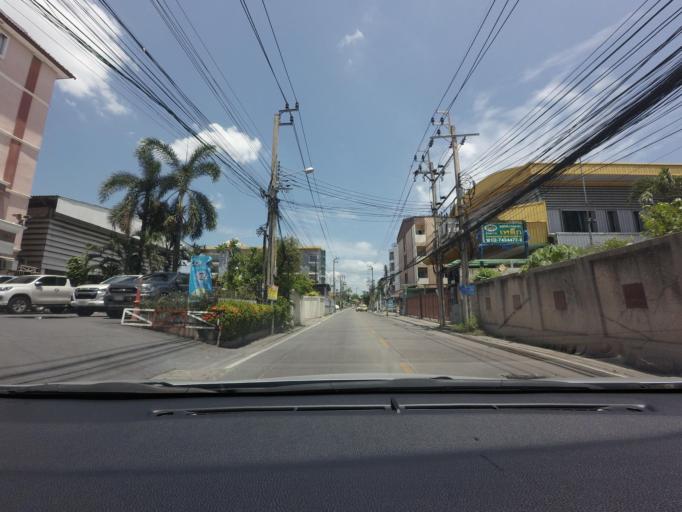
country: TH
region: Bangkok
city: Bang Na
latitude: 13.6893
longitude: 100.6395
